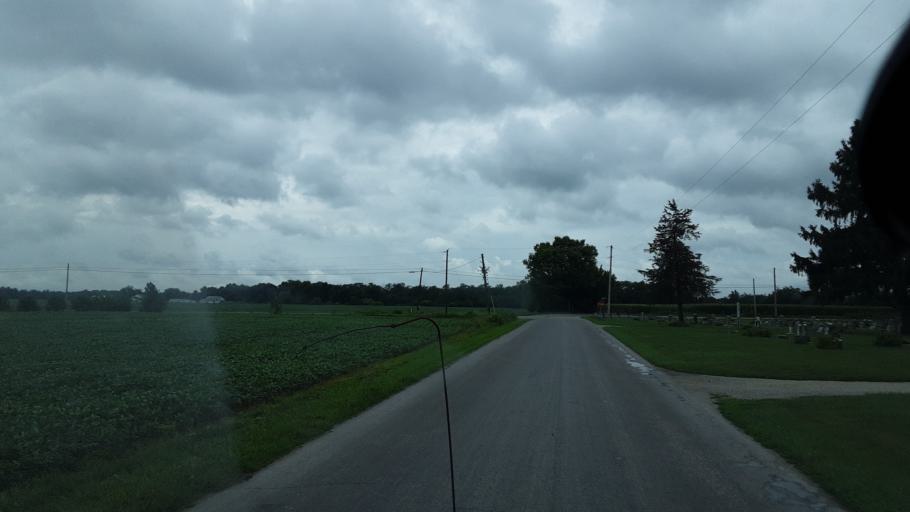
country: US
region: Indiana
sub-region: Adams County
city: Geneva
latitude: 40.5344
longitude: -84.9913
